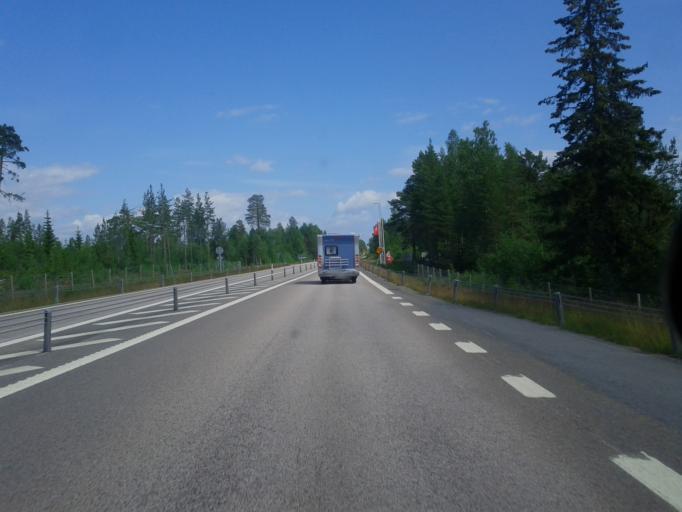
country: SE
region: Vaesternorrland
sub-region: OErnskoeldsviks Kommun
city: Husum
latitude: 63.4794
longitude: 19.2949
